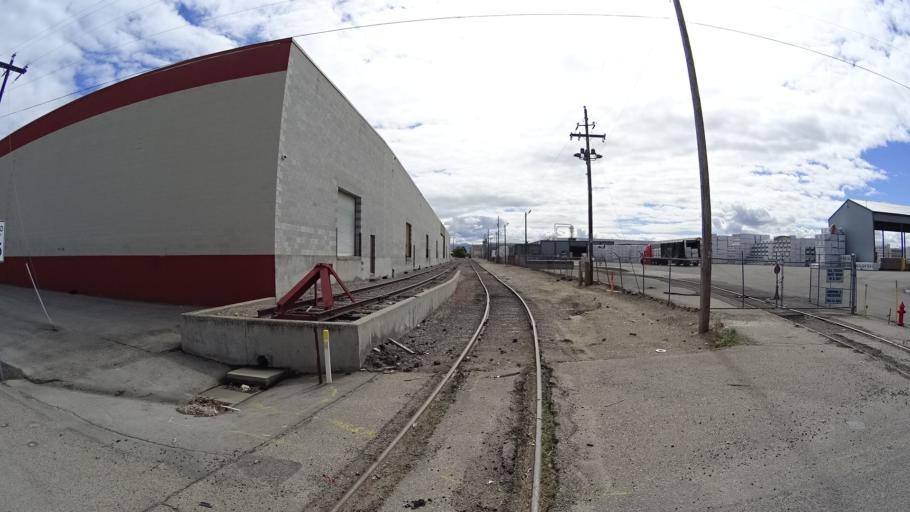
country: US
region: Idaho
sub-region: Ada County
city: Boise
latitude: 43.5591
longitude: -116.1934
